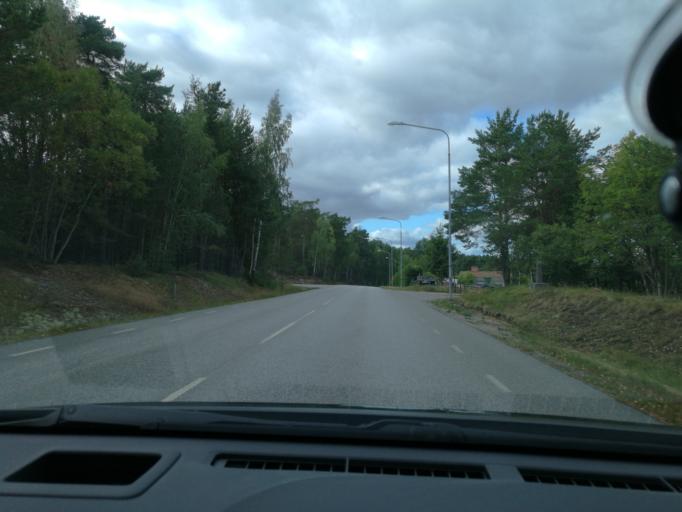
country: SE
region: Vaestmanland
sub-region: Kungsors Kommun
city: Kungsoer
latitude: 59.4116
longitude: 16.1074
